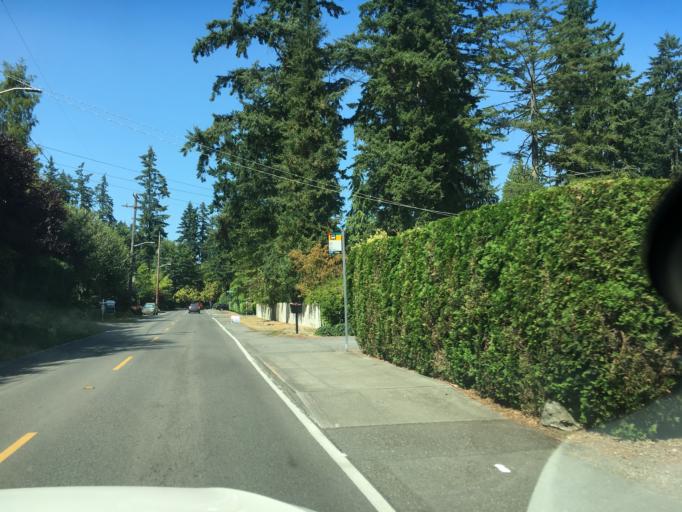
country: US
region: Washington
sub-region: King County
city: Shoreline
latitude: 47.7325
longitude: -122.3609
